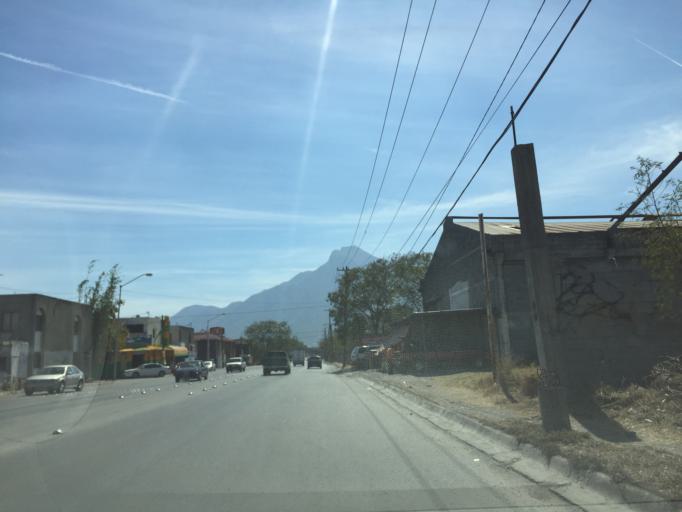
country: MX
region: Nuevo Leon
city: Guadalupe
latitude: 25.6982
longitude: -100.2400
